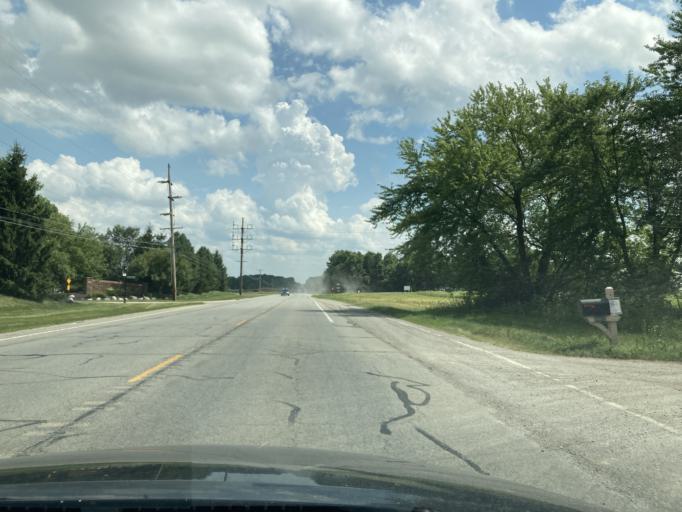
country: US
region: Indiana
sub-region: Boone County
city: Zionsville
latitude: 39.9920
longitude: -86.2615
